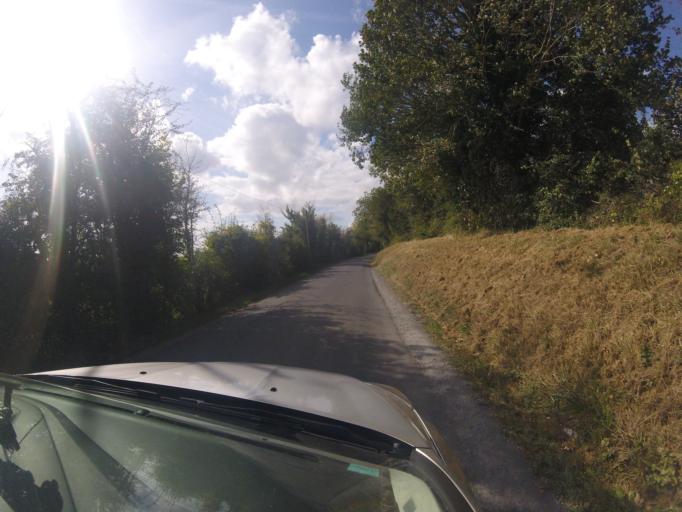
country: FR
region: Lower Normandy
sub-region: Departement du Calvados
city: Saint-Vigor-le-Grand
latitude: 49.3196
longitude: -0.6361
